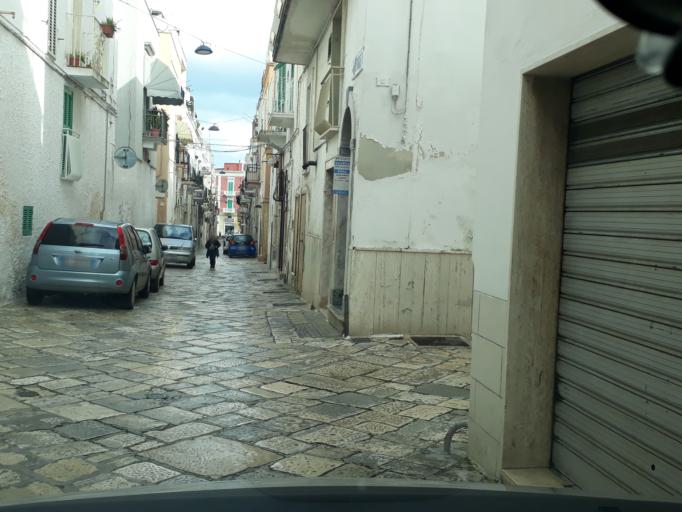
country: IT
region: Apulia
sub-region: Provincia di Brindisi
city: Fasano
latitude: 40.8370
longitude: 17.3590
